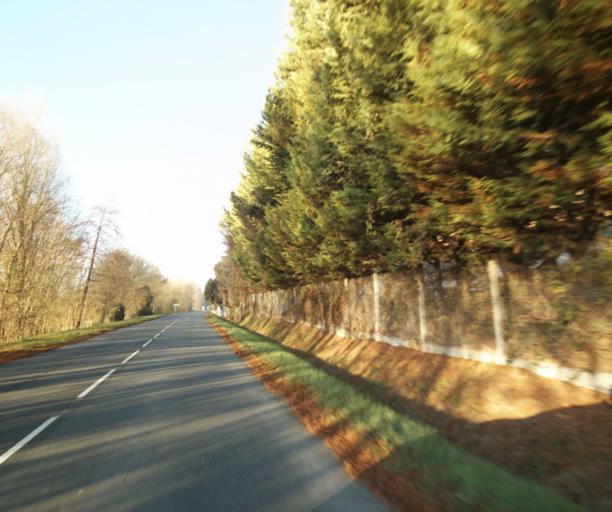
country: FR
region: Poitou-Charentes
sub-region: Departement de la Charente-Maritime
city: Cherac
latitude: 45.6873
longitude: -0.4176
